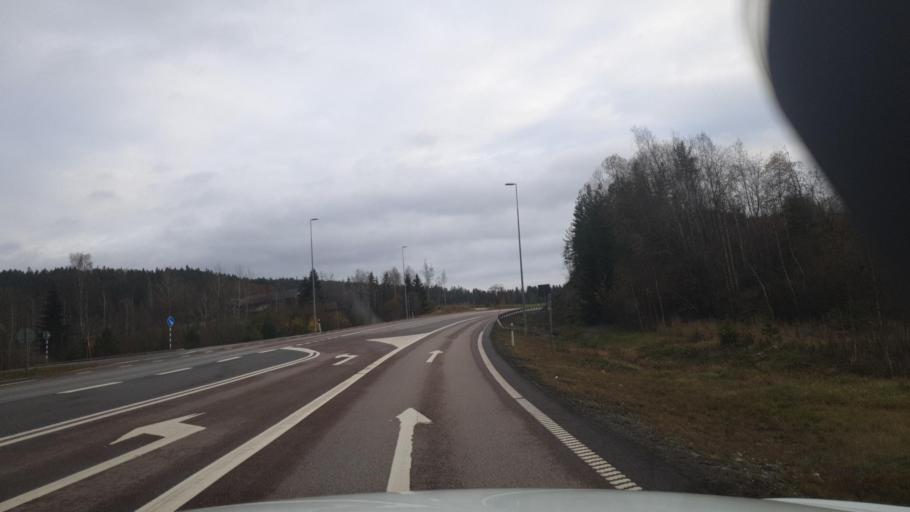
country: SE
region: Vaermland
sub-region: Arvika Kommun
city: Arvika
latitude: 59.6680
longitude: 12.7973
